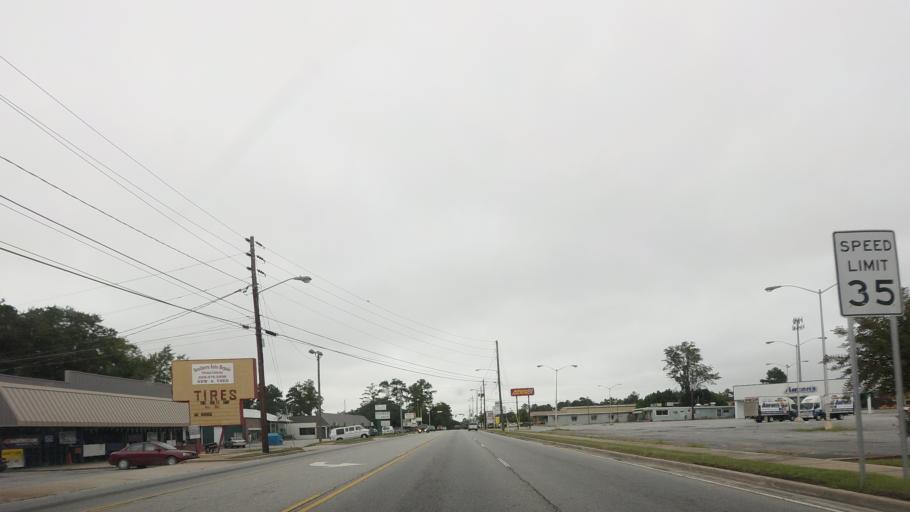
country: US
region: Georgia
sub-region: Lowndes County
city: Valdosta
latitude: 30.8587
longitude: -83.2814
